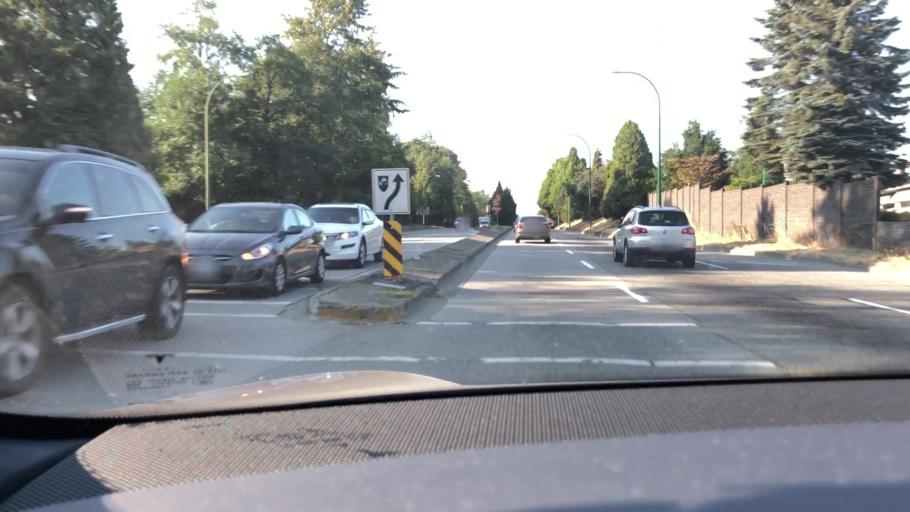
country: CA
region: British Columbia
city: Burnaby
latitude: 49.2149
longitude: -123.0237
